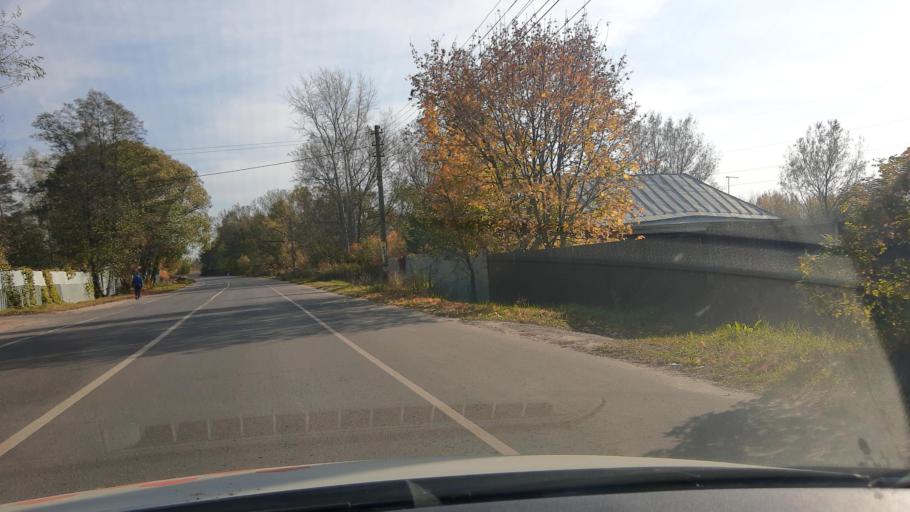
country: RU
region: Moskovskaya
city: Fryazevo
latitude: 55.7302
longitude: 38.4615
